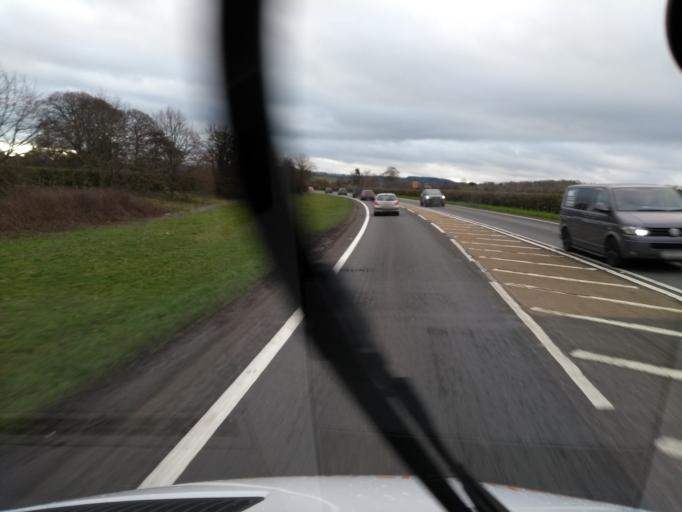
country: GB
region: England
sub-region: Somerset
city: Ilminster
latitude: 50.9398
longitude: -2.9503
